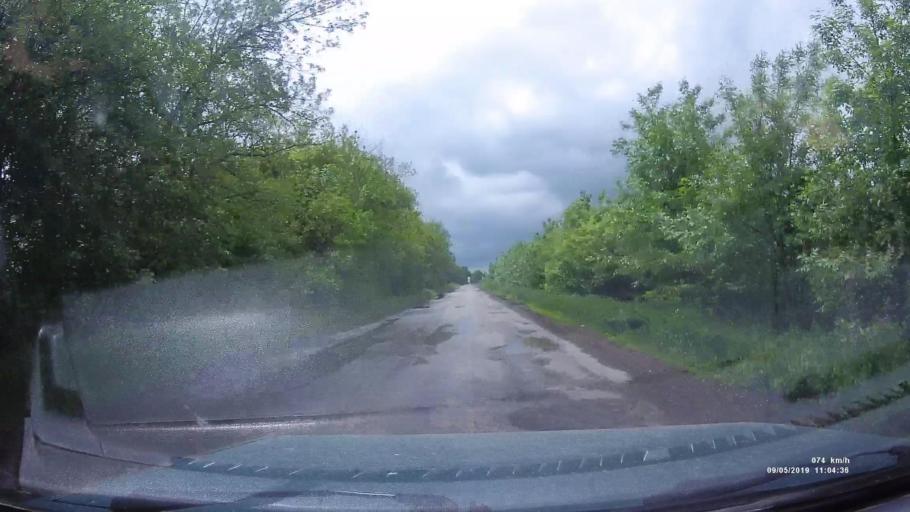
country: RU
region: Krasnodarskiy
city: Kanelovskaya
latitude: 46.8152
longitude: 39.2099
